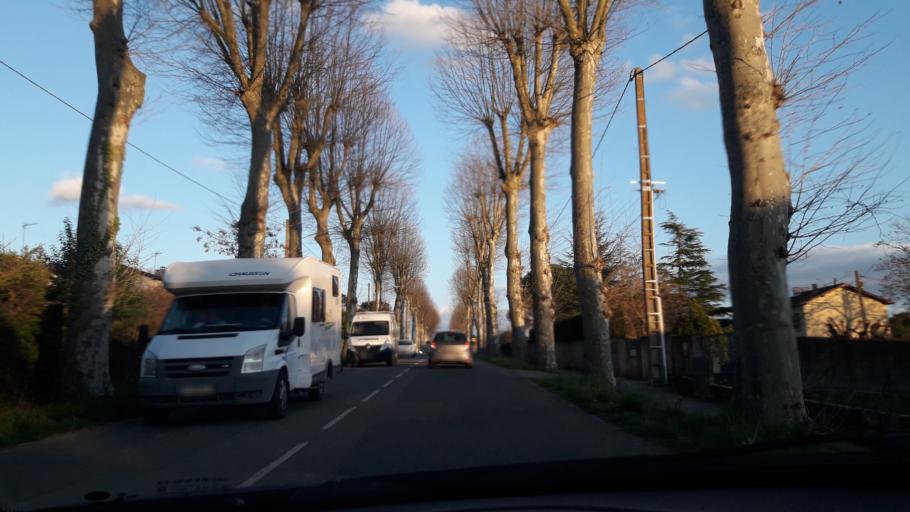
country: FR
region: Midi-Pyrenees
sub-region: Departement du Gers
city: Pujaudran
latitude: 43.6124
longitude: 1.0923
